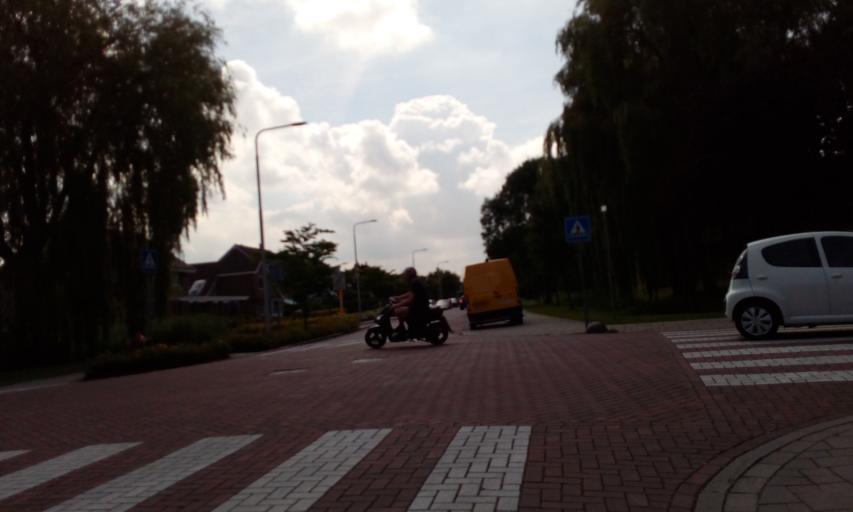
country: NL
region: South Holland
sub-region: Gemeente Den Haag
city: Ypenburg
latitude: 52.0462
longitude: 4.3957
